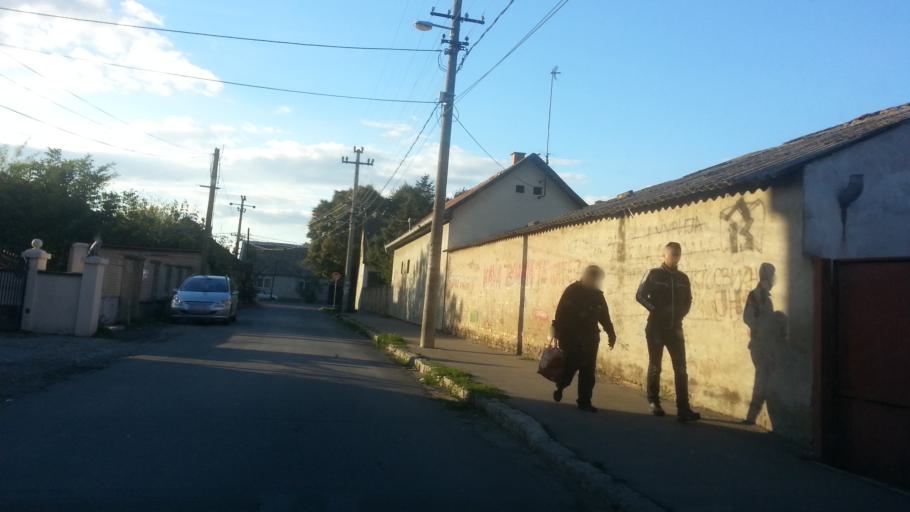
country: RS
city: Novi Banovci
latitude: 44.9069
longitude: 20.2773
